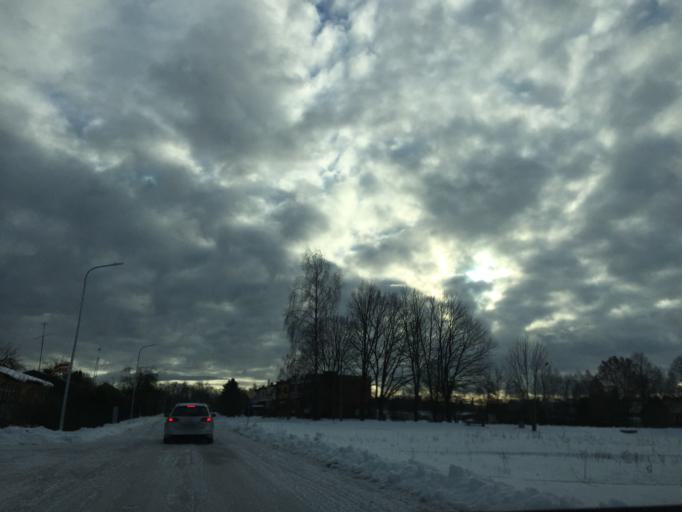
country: LV
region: Lielvarde
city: Lielvarde
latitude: 56.6350
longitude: 24.7516
